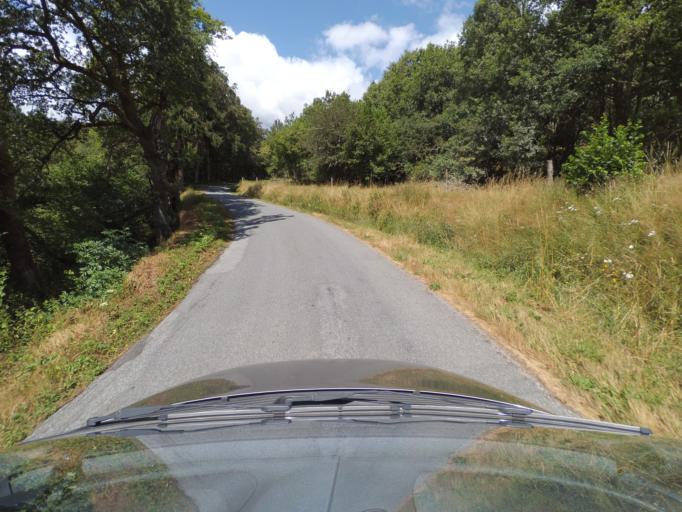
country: FR
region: Limousin
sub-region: Departement de la Creuse
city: Banize
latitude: 45.7923
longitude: 1.9338
